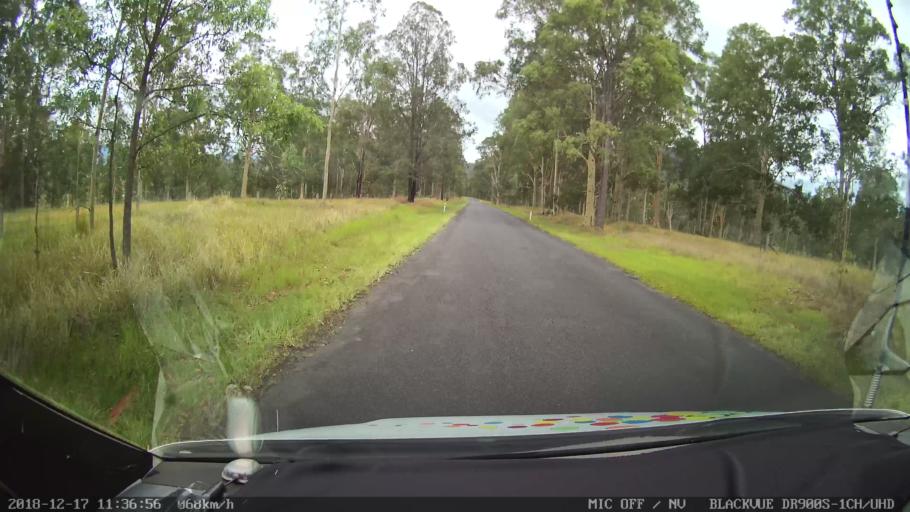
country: AU
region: New South Wales
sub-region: Kyogle
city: Kyogle
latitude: -28.7094
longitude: 152.6062
